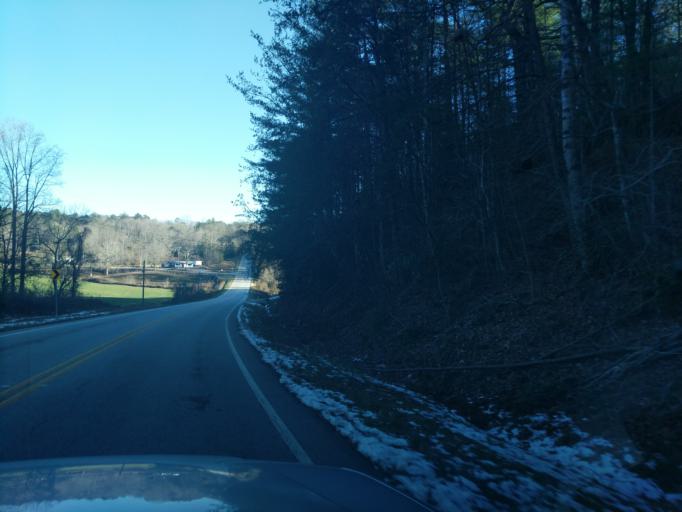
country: US
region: Georgia
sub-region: Rabun County
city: Clayton
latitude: 34.8456
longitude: -83.3422
